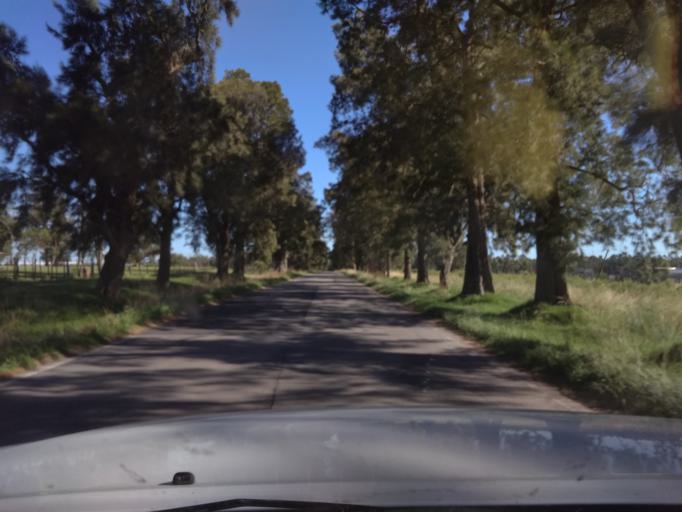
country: UY
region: Canelones
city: San Bautista
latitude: -34.3856
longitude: -55.9595
